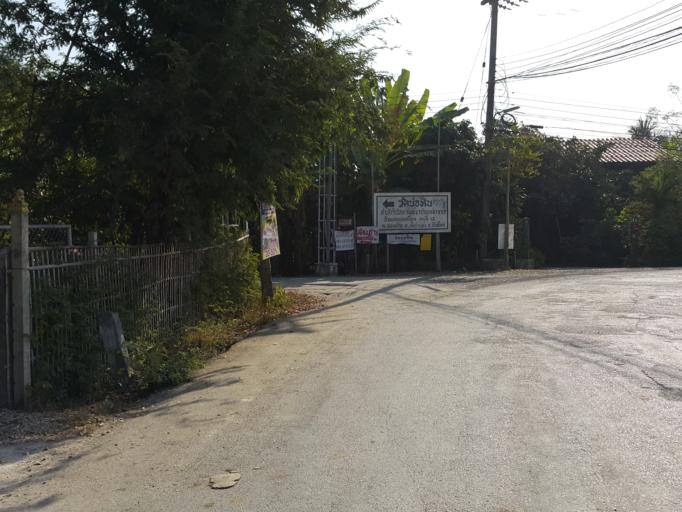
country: TH
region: Chiang Mai
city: San Kamphaeng
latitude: 18.6962
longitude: 99.1124
